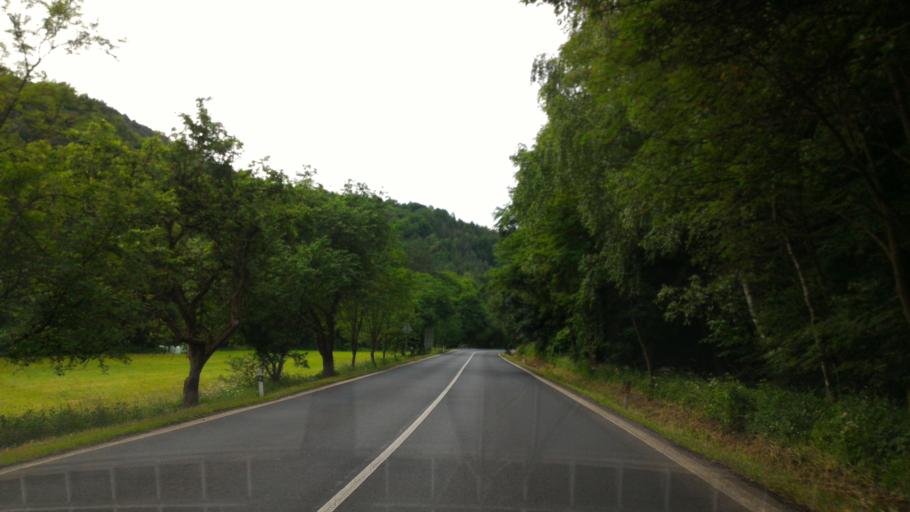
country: CZ
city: Duba
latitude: 50.5070
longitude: 14.4883
